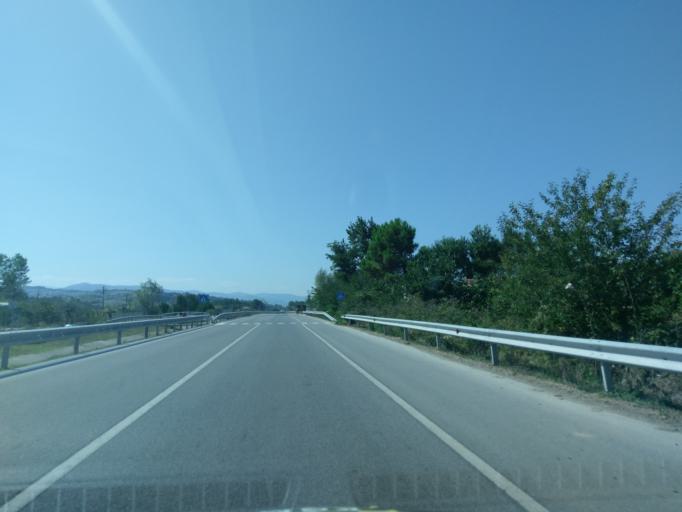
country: TR
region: Samsun
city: Alacam
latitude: 41.6091
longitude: 35.6601
